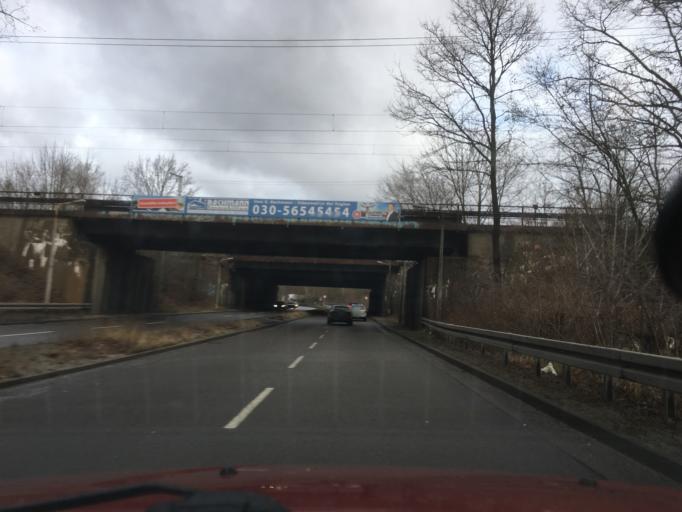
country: DE
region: Berlin
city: Grunau
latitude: 52.4152
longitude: 13.5682
